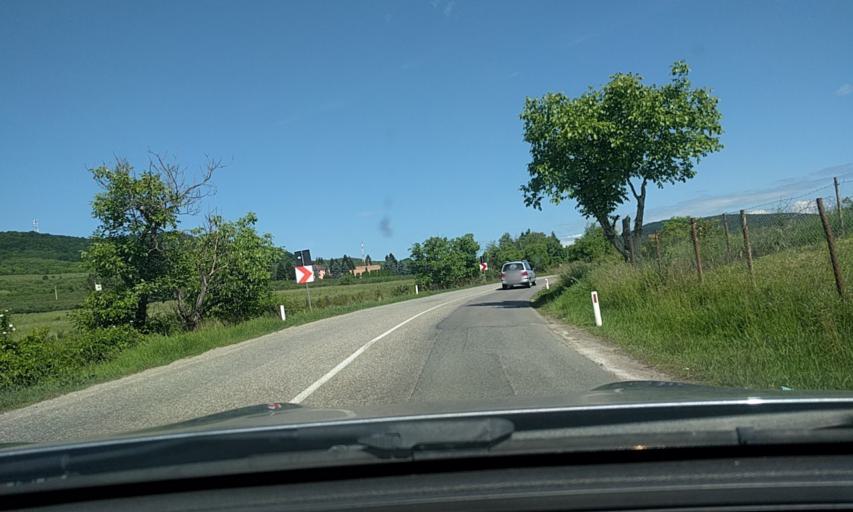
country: RO
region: Bistrita-Nasaud
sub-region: Municipiul Bistrita
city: Unirea
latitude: 47.1633
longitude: 24.5019
